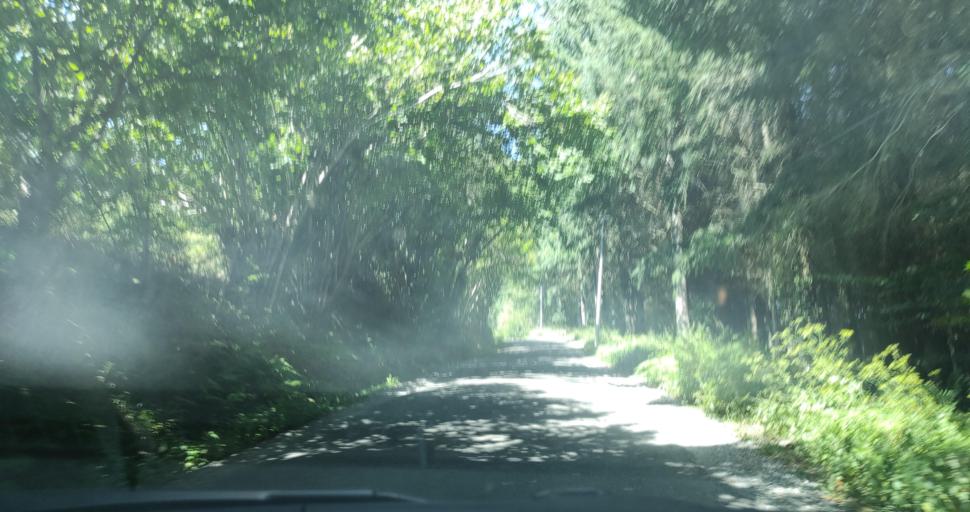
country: FR
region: Midi-Pyrenees
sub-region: Departement de l'Aveyron
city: Firmi
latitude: 44.5194
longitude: 2.3151
